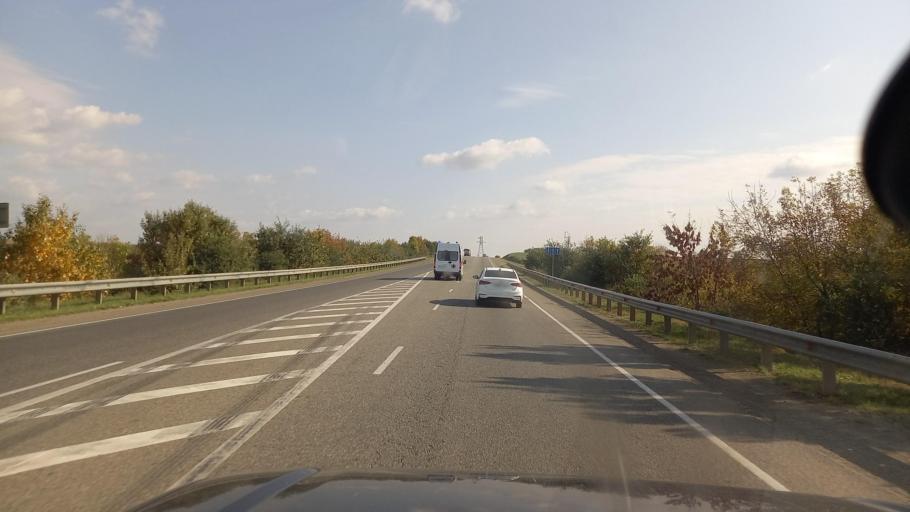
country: RU
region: Krasnodarskiy
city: Kholmskiy
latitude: 44.8546
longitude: 38.3453
